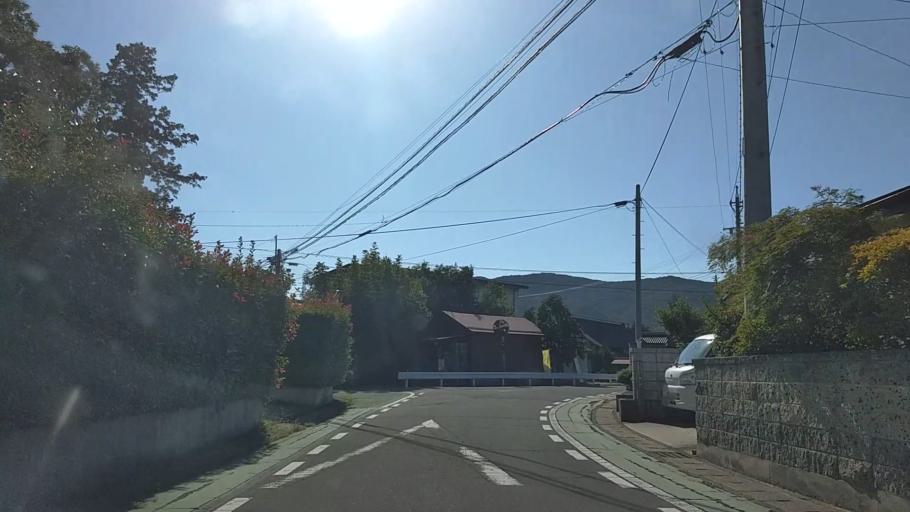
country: JP
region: Nagano
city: Nagano-shi
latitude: 36.6003
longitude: 138.1405
